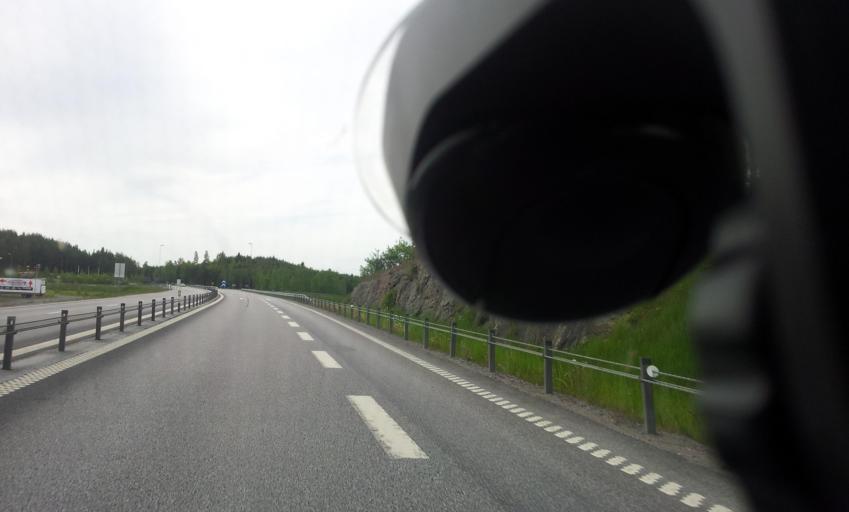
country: SE
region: OEstergoetland
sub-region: Valdemarsviks Kommun
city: Valdemarsvik
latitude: 58.2242
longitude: 16.5526
